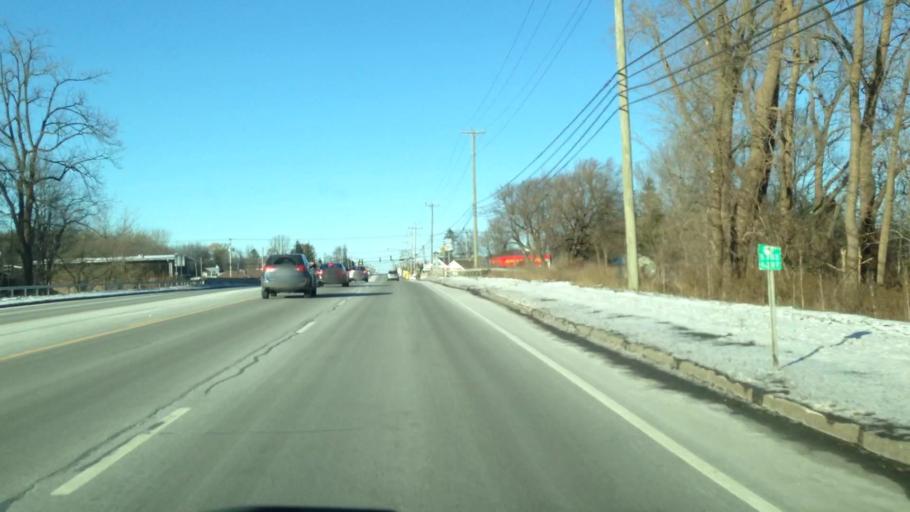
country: US
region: New York
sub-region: Erie County
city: Depew
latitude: 42.8581
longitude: -78.6969
